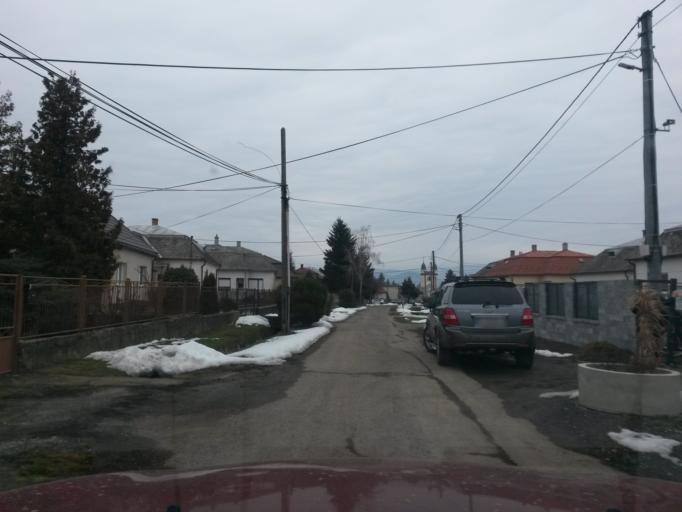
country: SK
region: Kosicky
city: Vinne
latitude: 48.7582
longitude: 21.9937
